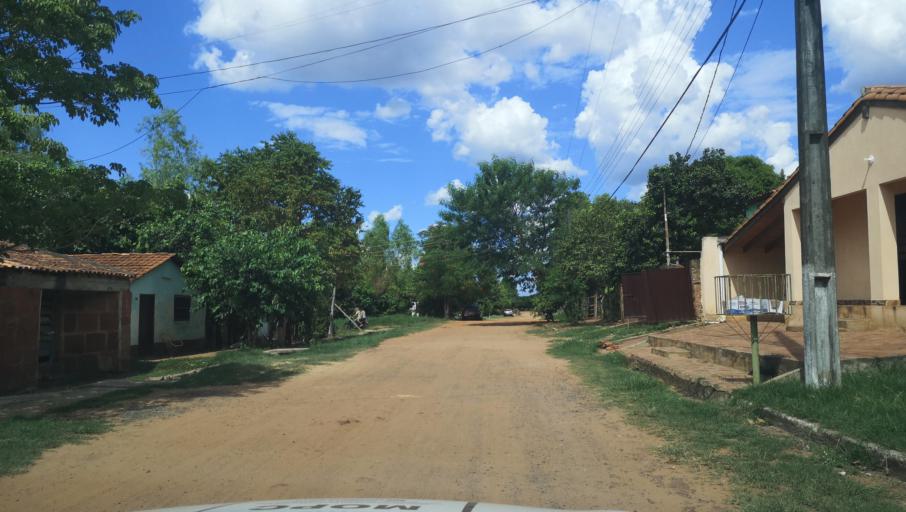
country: PY
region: Misiones
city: Santa Maria
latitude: -26.8876
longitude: -57.0096
